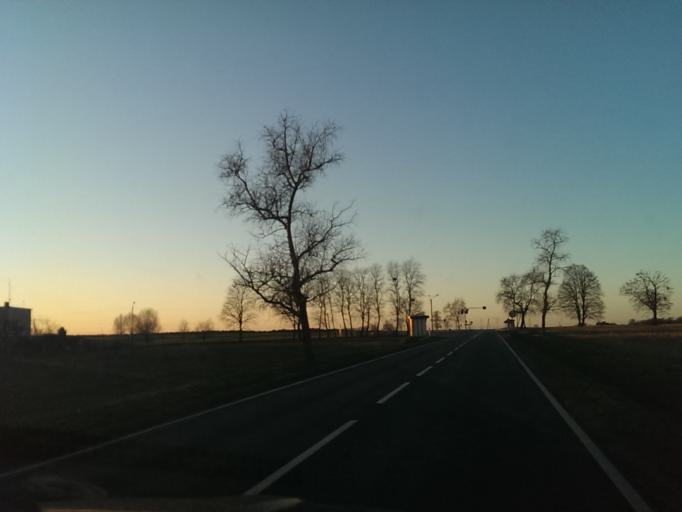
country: PL
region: Kujawsko-Pomorskie
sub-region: Powiat nakielski
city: Naklo nad Notecia
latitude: 53.0963
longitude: 17.6486
